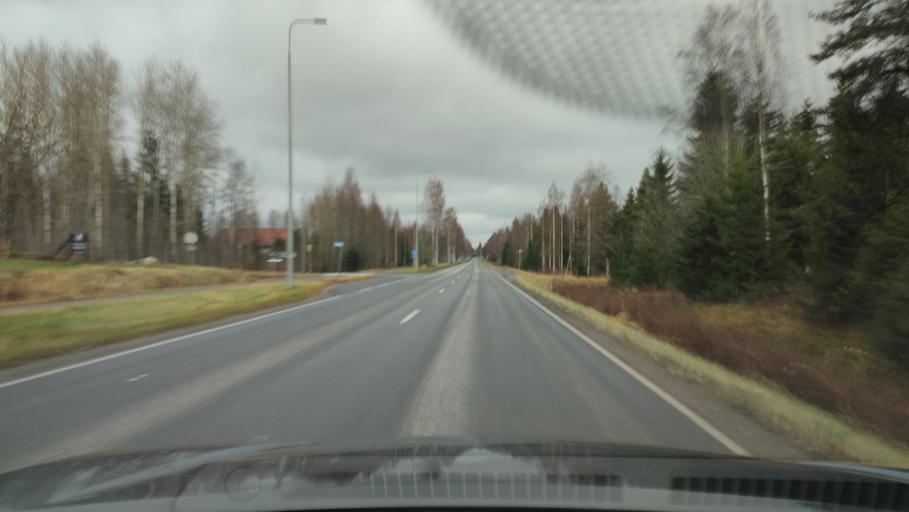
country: FI
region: Southern Ostrobothnia
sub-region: Suupohja
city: Kauhajoki
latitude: 62.4095
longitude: 22.1669
